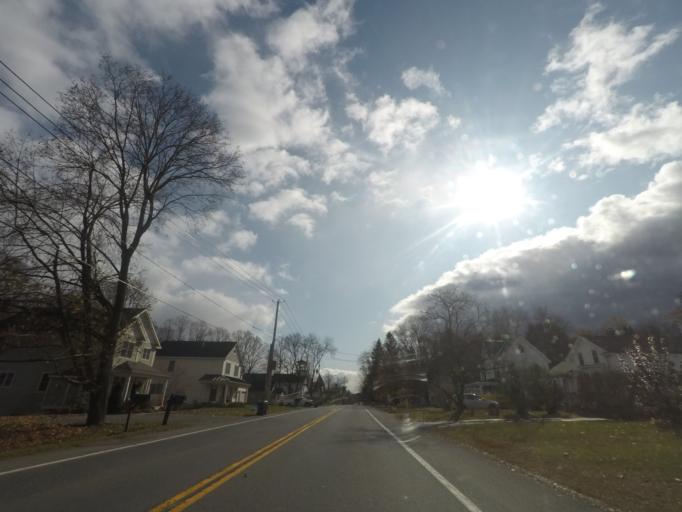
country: US
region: New York
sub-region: Saratoga County
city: Country Knolls
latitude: 42.9085
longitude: -73.8228
